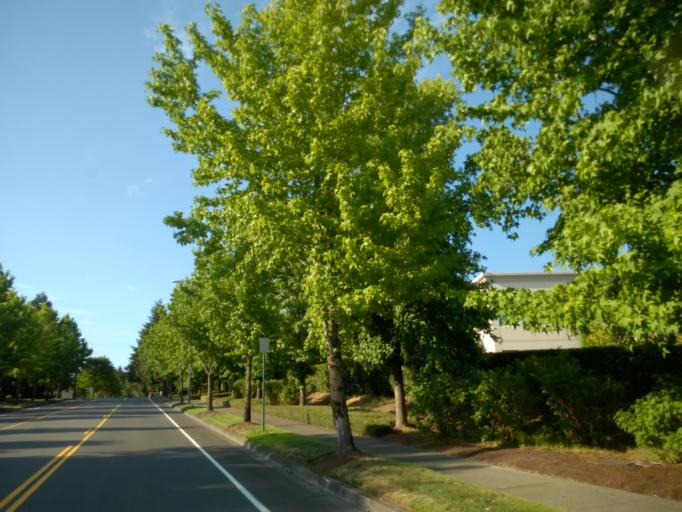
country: US
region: Washington
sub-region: King County
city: Bothell
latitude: 47.7794
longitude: -122.1858
